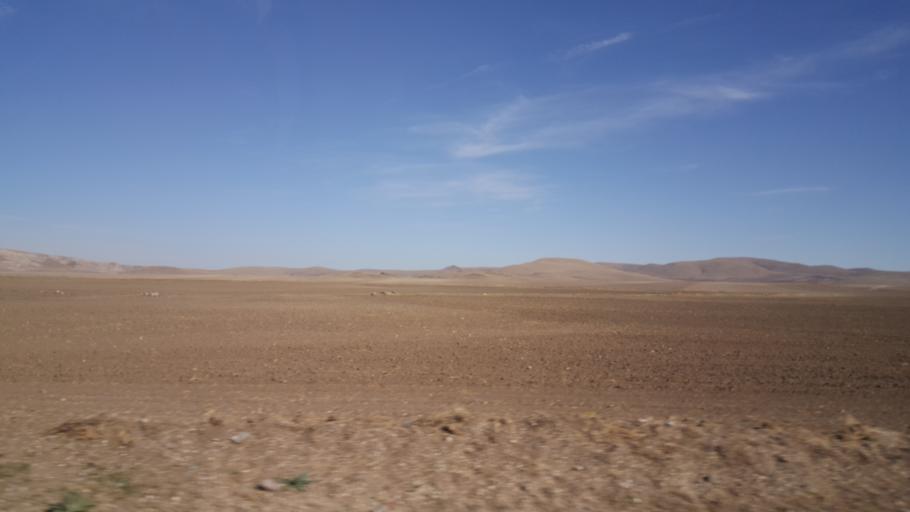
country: TR
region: Ankara
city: Yenice
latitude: 39.3029
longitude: 32.7570
